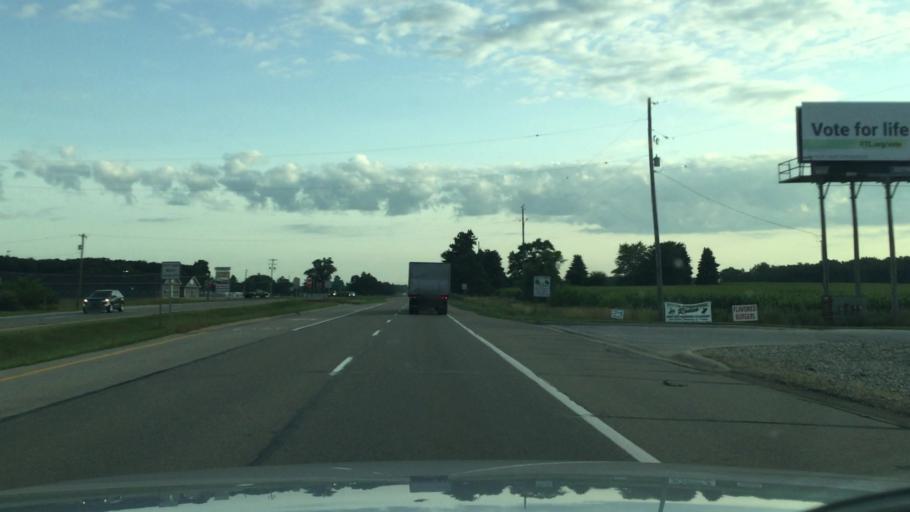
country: US
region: Michigan
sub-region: Clinton County
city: Saint Johns
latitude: 43.0608
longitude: -84.5637
